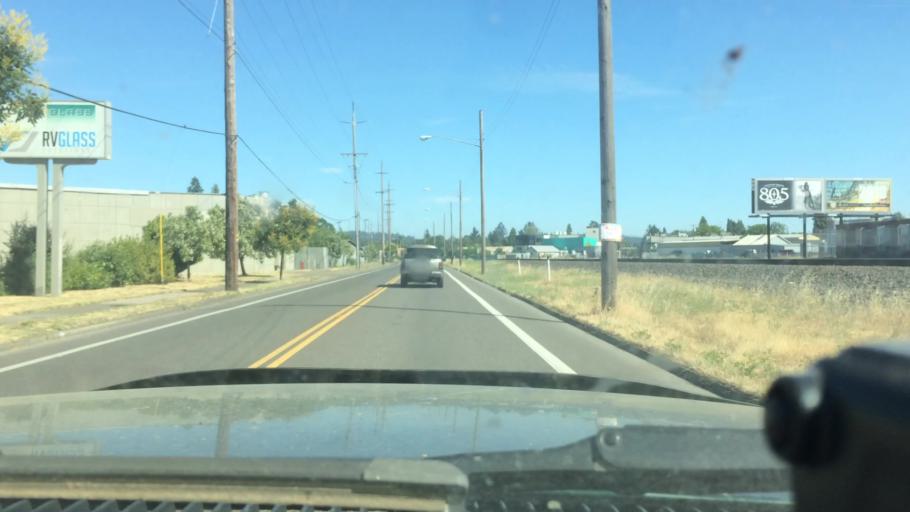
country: US
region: Oregon
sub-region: Lane County
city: Eugene
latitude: 44.0612
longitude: -123.1149
